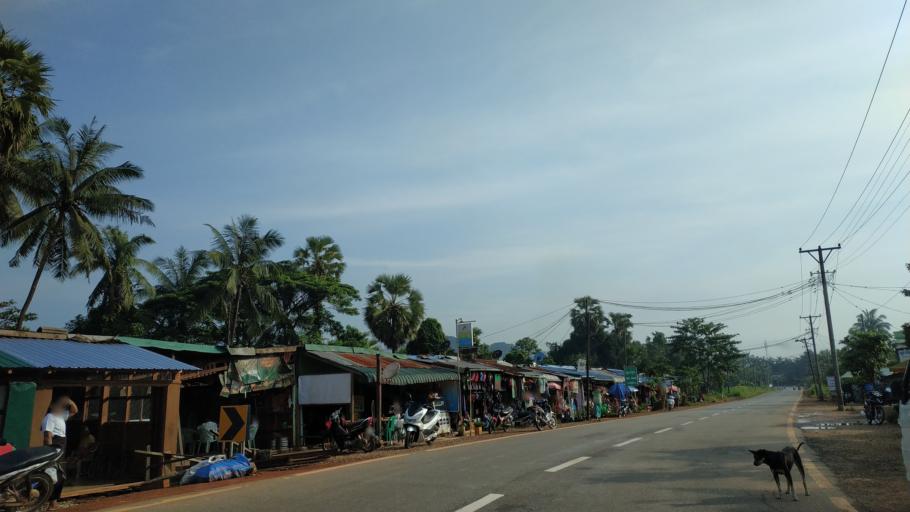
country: MM
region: Tanintharyi
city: Dawei
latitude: 14.2464
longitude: 98.2017
